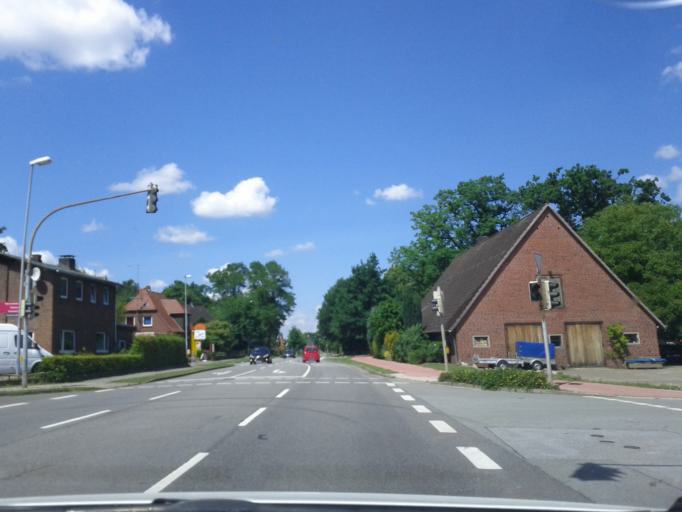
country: DE
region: Lower Saxony
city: Agathenburg
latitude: 53.5618
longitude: 9.5308
